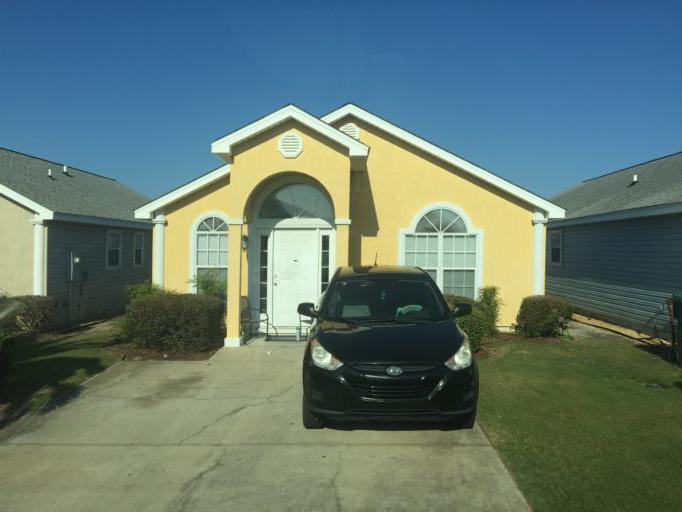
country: US
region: Florida
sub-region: Bay County
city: Panama City Beach
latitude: 30.1939
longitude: -85.8199
